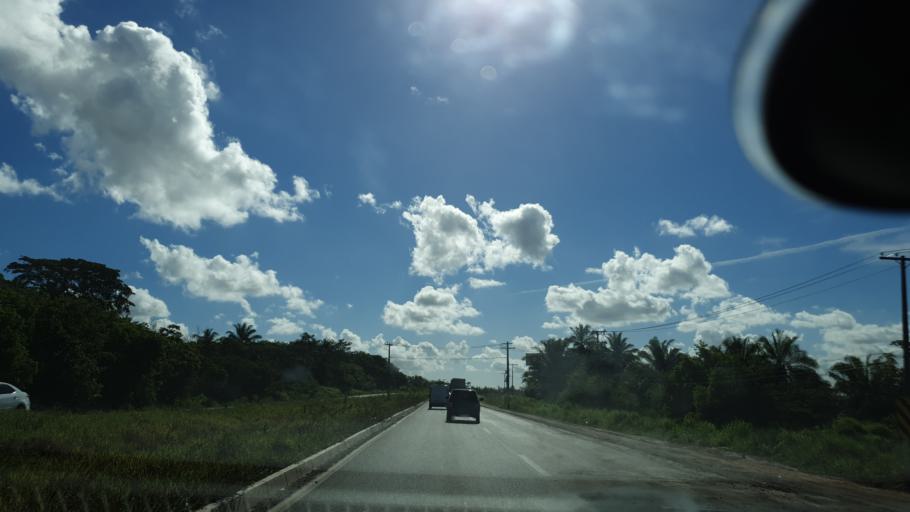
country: BR
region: Bahia
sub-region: Camacari
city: Camacari
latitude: -12.6812
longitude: -38.2869
